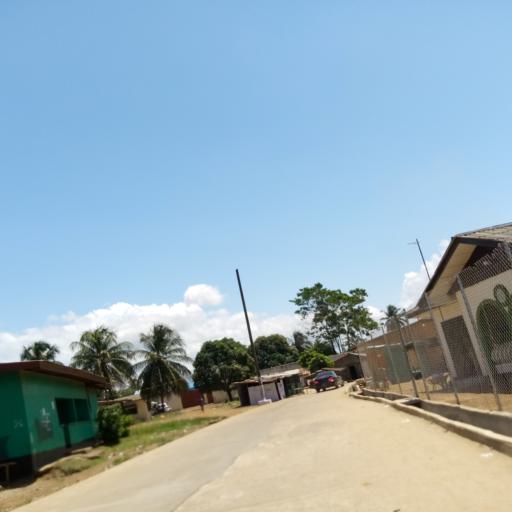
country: LR
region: Montserrado
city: Monrovia
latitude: 6.2433
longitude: -10.6940
